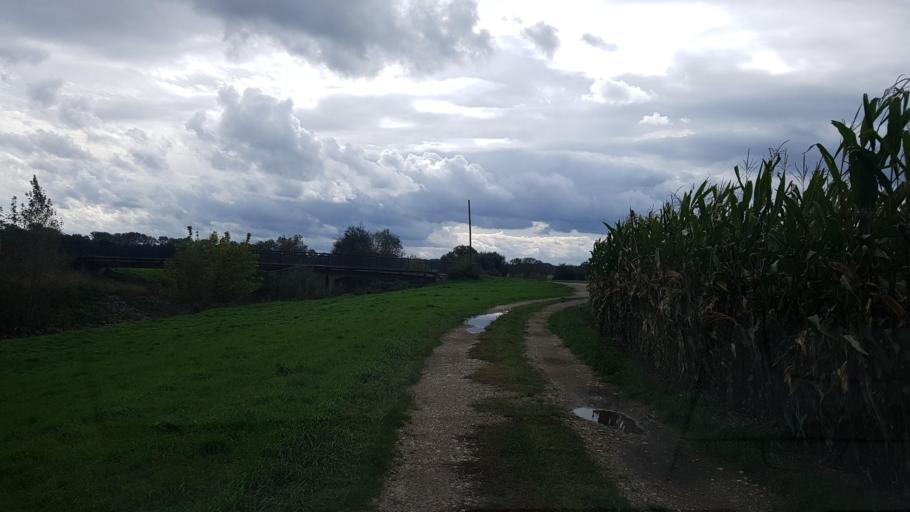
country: DE
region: Saxony
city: Elstertrebnitz
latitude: 51.1440
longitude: 12.2552
